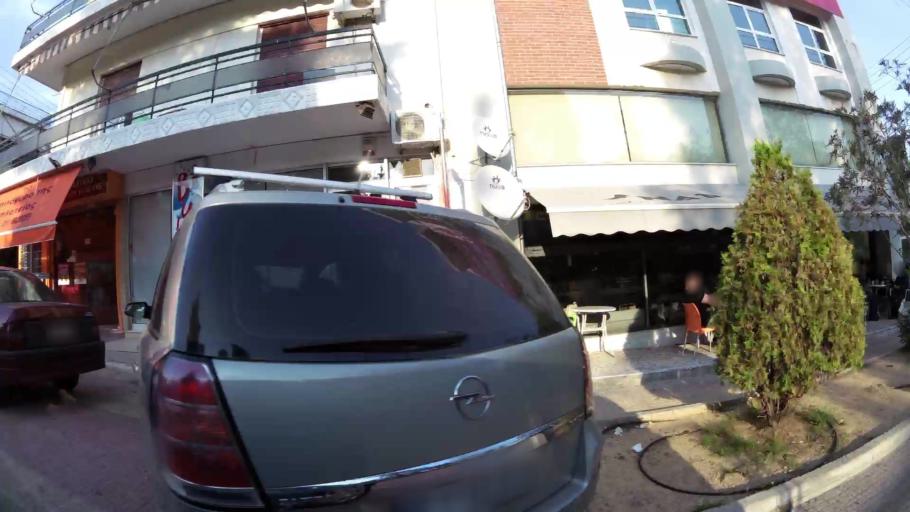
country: GR
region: Attica
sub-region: Nomarchia Athinas
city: Petroupolis
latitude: 38.0392
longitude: 23.6712
